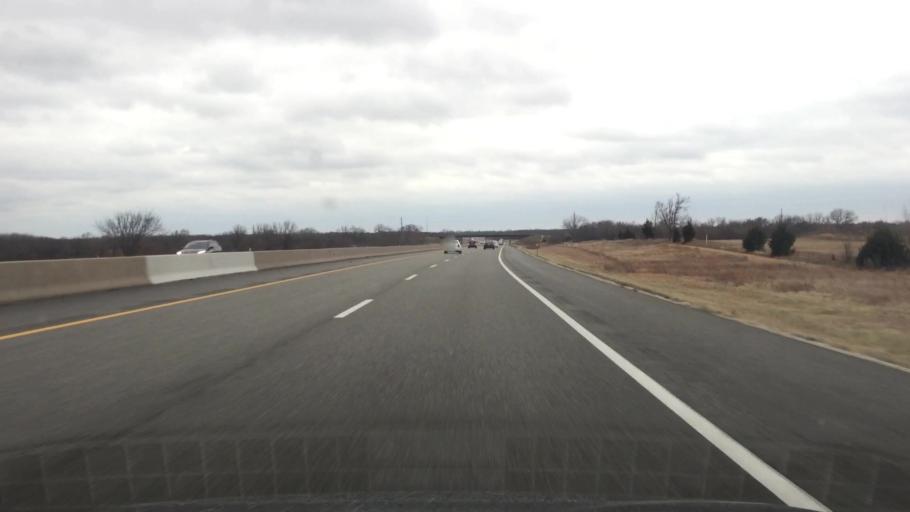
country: US
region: Kansas
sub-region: Butler County
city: Andover
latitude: 37.7361
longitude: -97.0703
